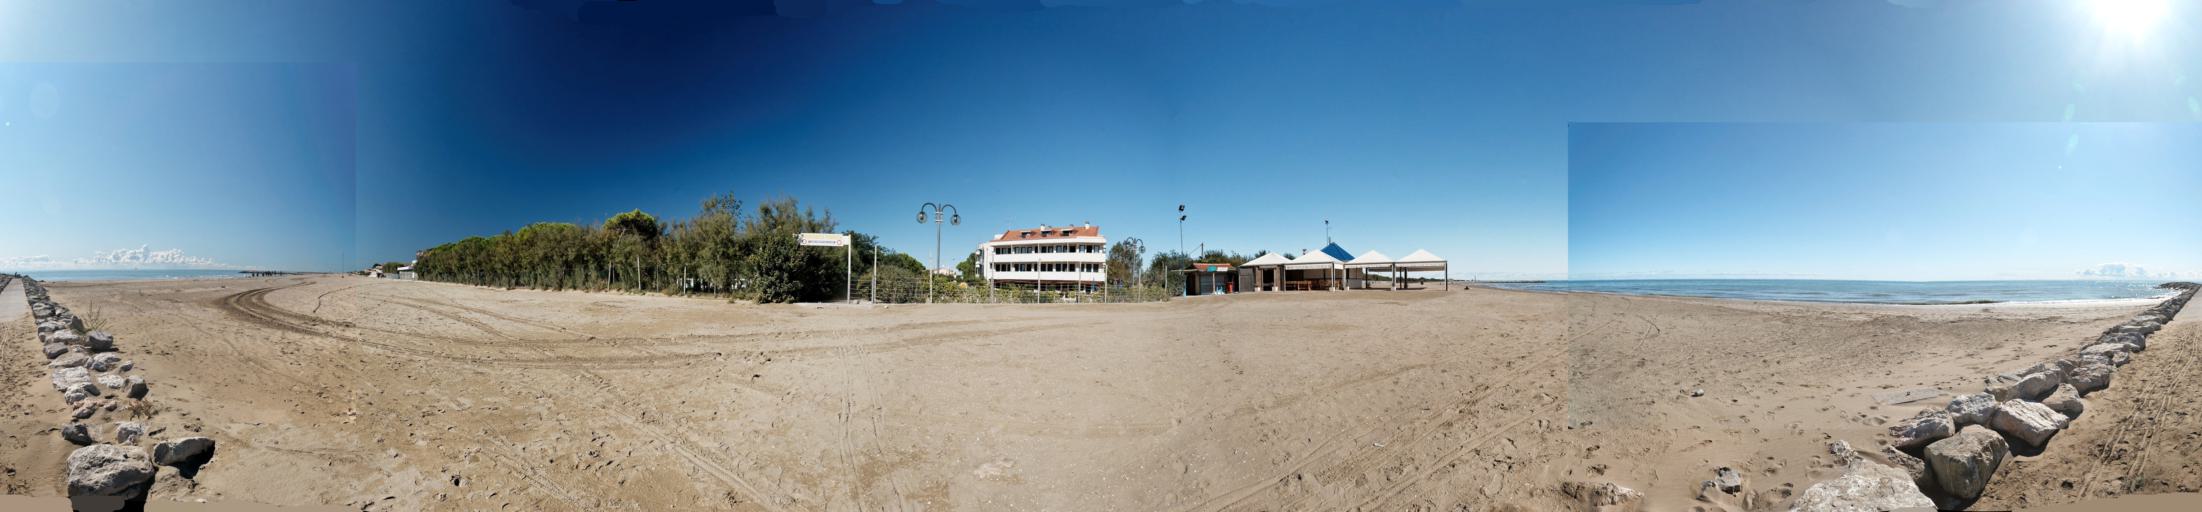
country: IT
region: Veneto
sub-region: Provincia di Venezia
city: Cavallino
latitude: 45.4693
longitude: 12.5474
